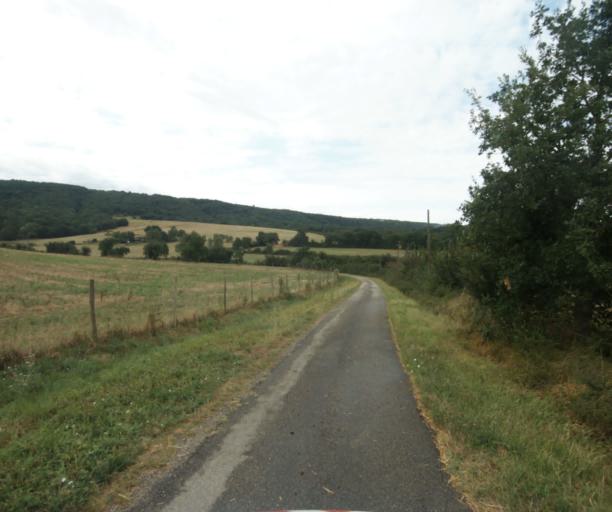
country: FR
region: Midi-Pyrenees
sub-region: Departement de la Haute-Garonne
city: Revel
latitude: 43.4268
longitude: 1.9978
